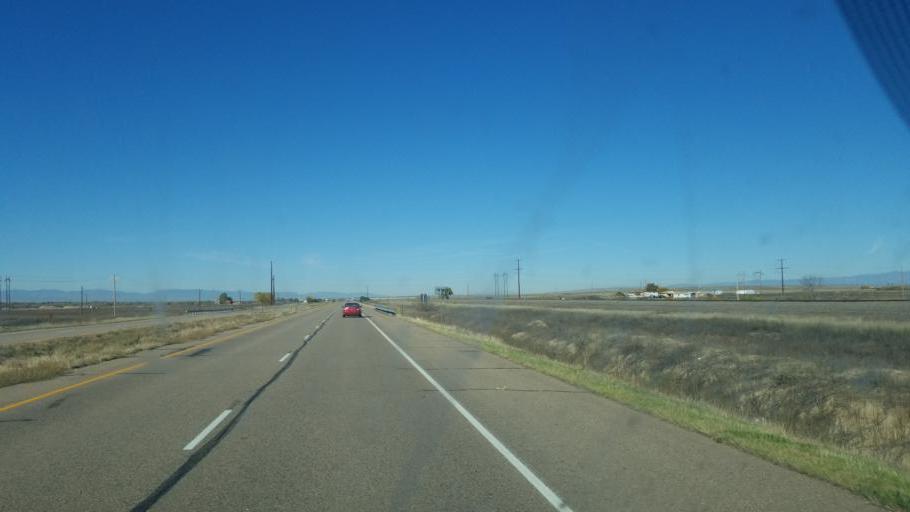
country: US
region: Colorado
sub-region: Pueblo County
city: Pueblo
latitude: 38.2677
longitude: -104.3793
